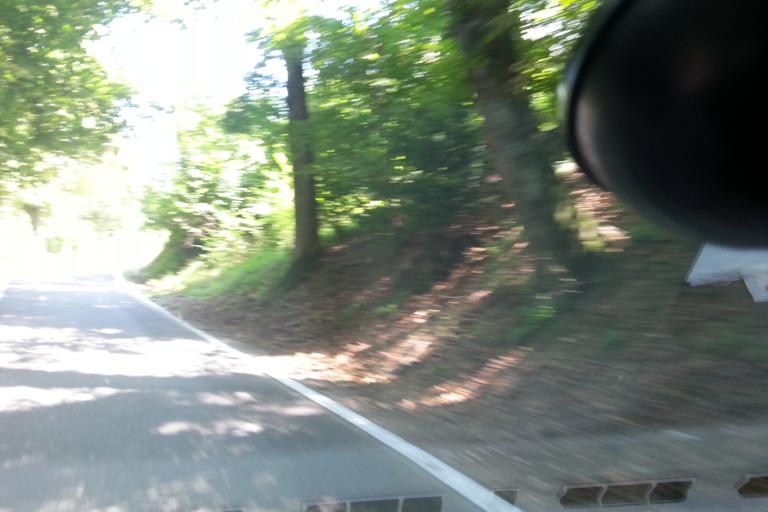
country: IT
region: Piedmont
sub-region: Provincia di Torino
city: Chiusa di San Michele
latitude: 45.0949
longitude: 7.3450
